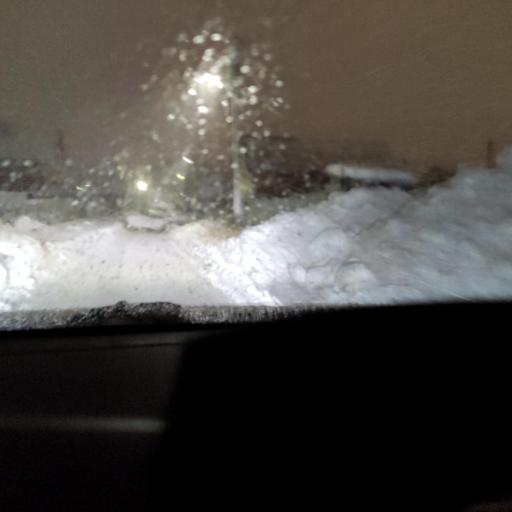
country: RU
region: Tatarstan
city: Stolbishchi
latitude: 55.7493
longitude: 49.2856
